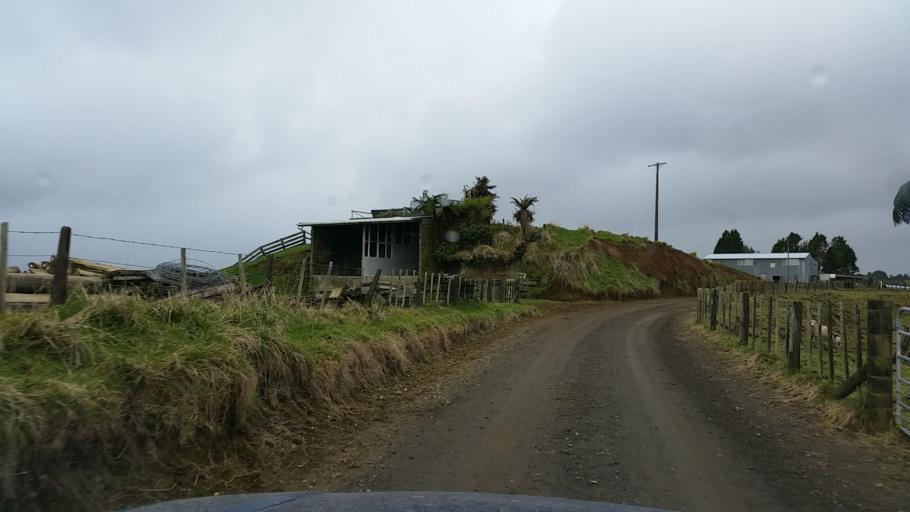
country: NZ
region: Taranaki
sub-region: South Taranaki District
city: Eltham
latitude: -39.1670
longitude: 174.6280
